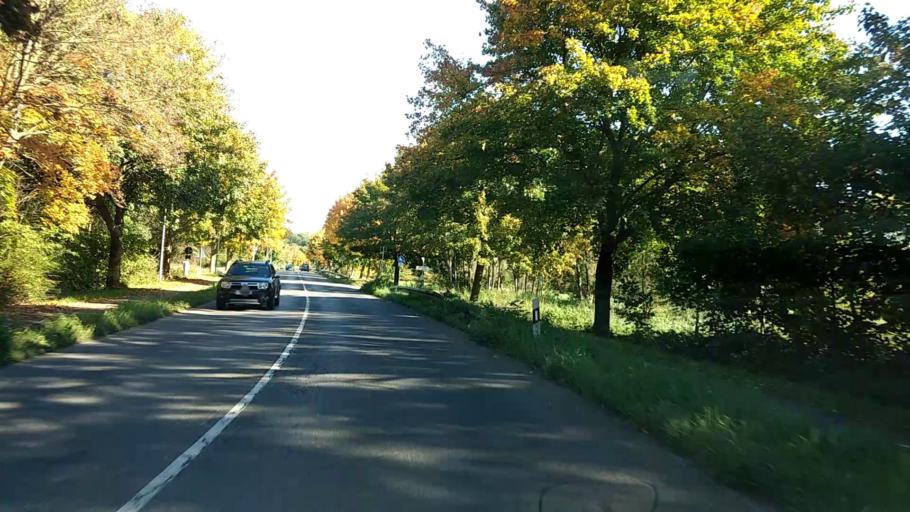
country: DE
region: North Rhine-Westphalia
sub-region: Regierungsbezirk Koln
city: Kerpen
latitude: 50.9130
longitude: 6.6933
